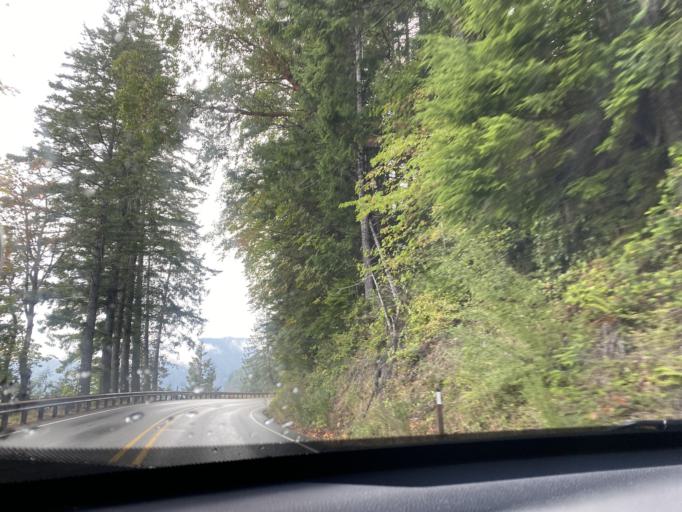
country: CA
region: British Columbia
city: Sooke
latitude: 48.0588
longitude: -123.7828
